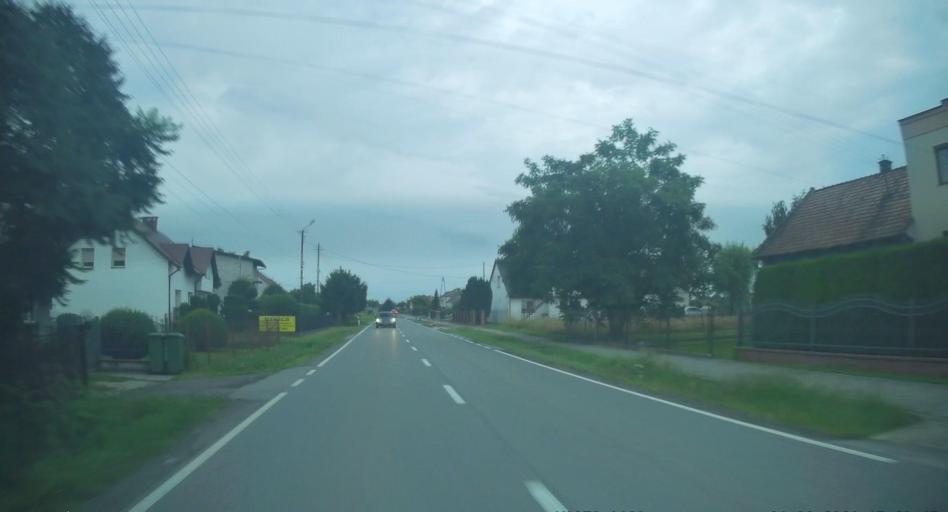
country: PL
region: Lesser Poland Voivodeship
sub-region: Powiat tarnowski
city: Wierzchoslawice
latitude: 49.9996
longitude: 20.8542
